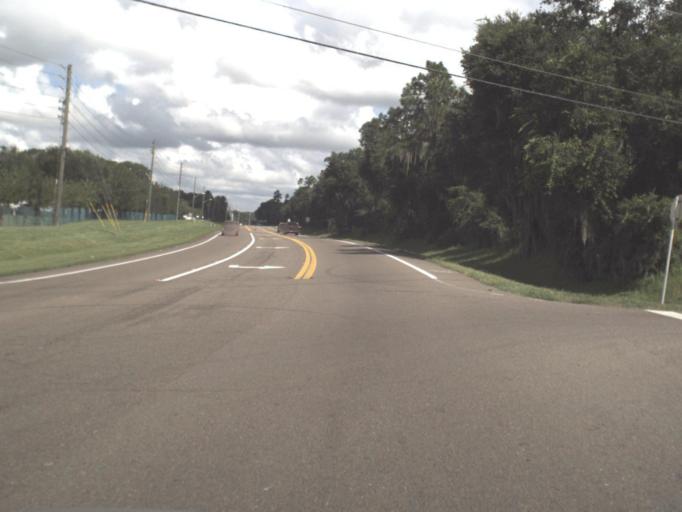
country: US
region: Florida
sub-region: Polk County
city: Winston
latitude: 28.0211
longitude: -82.0147
